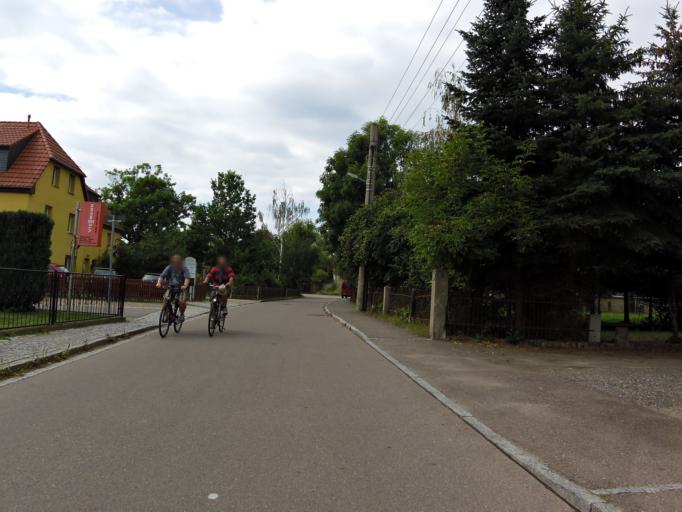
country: DE
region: Saxony
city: Radebeul
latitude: 51.0926
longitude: 13.6449
